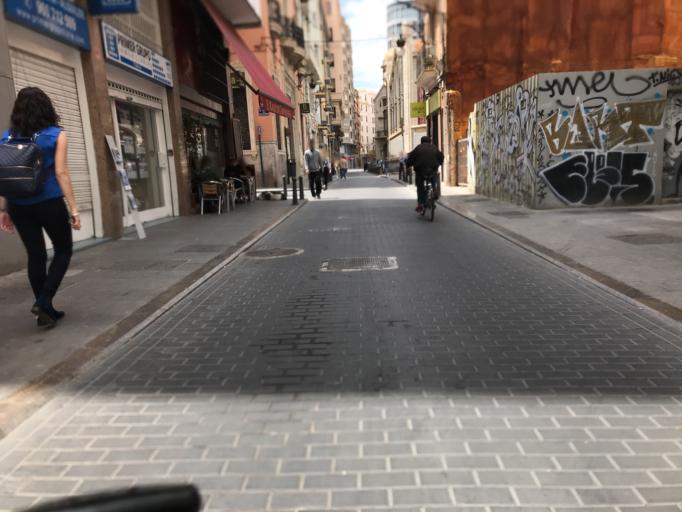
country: ES
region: Valencia
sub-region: Provincia de Valencia
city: Valencia
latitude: 39.4730
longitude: -0.3780
